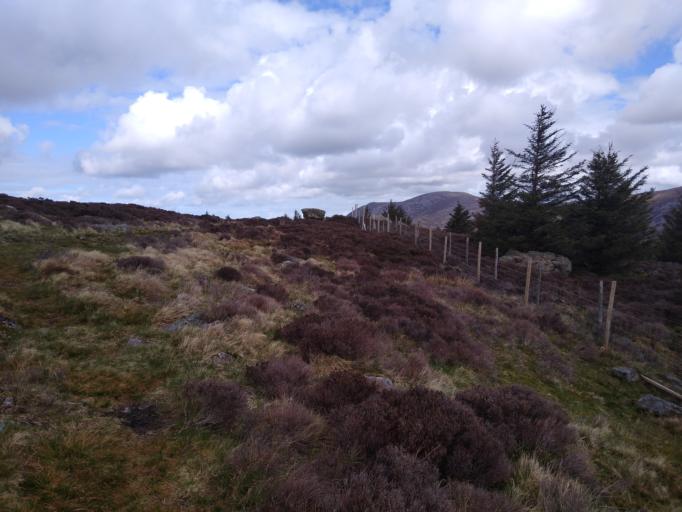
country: GB
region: England
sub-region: Cumbria
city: Cockermouth
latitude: 54.5052
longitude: -3.3238
